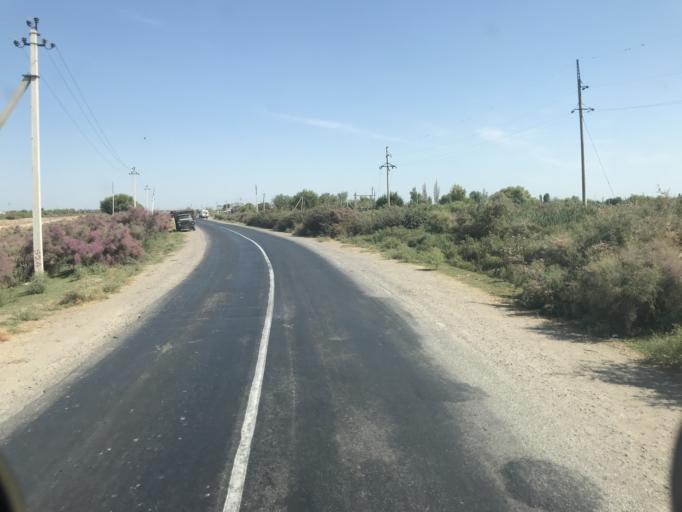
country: KZ
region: Ongtustik Qazaqstan
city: Myrzakent
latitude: 40.7280
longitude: 68.5363
